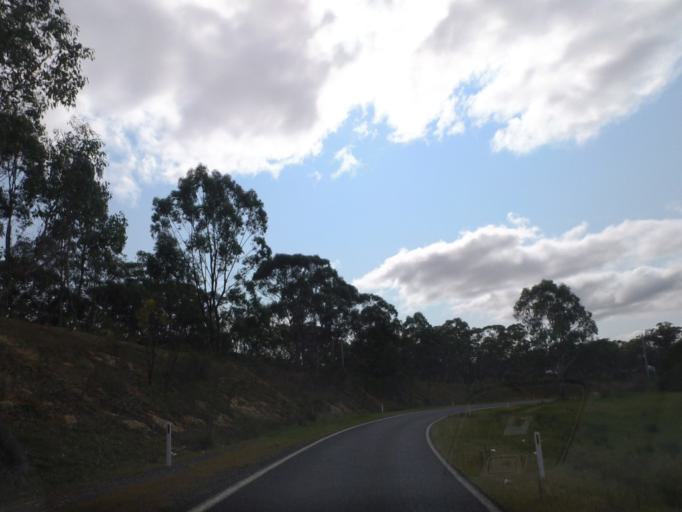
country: AU
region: Victoria
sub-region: Murrindindi
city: Kinglake West
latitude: -37.1088
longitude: 145.0901
